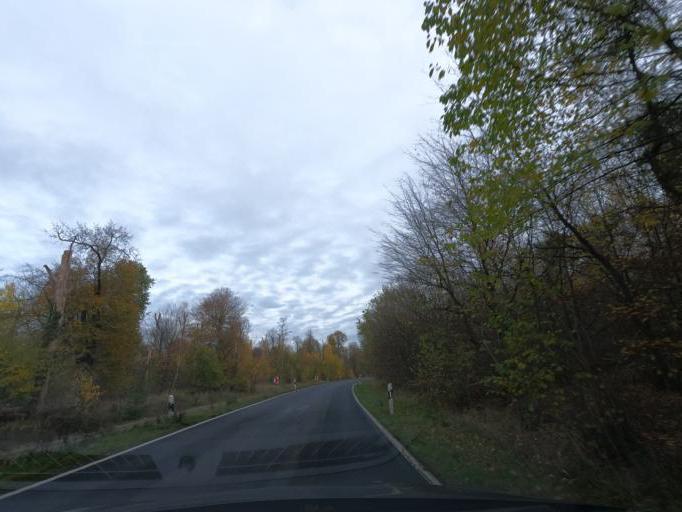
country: DE
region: Lower Saxony
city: Braunschweig
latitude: 52.3173
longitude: 10.5731
